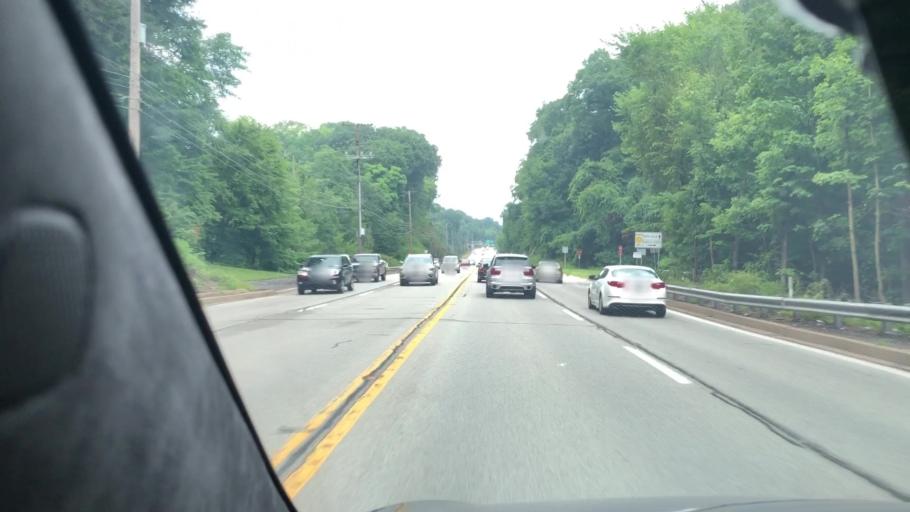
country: US
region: Pennsylvania
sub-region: Allegheny County
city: Churchill
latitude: 40.4347
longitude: -79.8229
